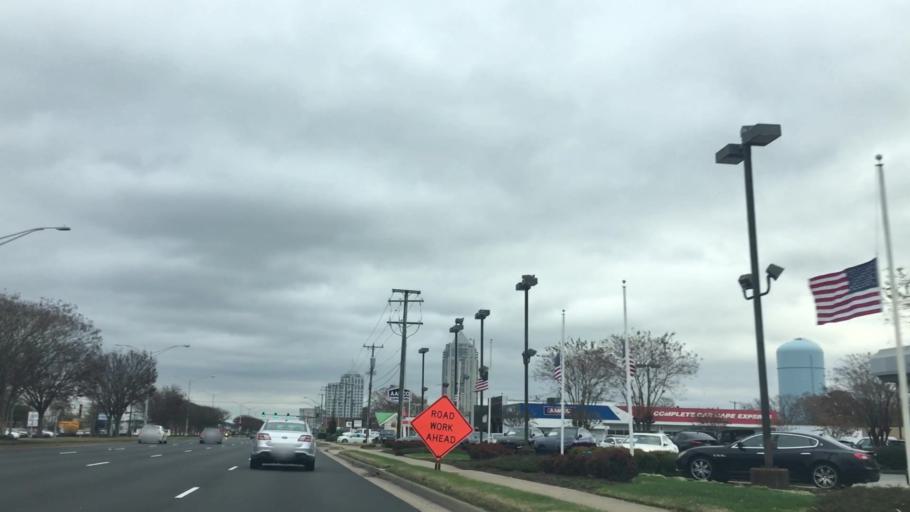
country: US
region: Virginia
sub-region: City of Chesapeake
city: Chesapeake
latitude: 36.8436
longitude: -76.1489
